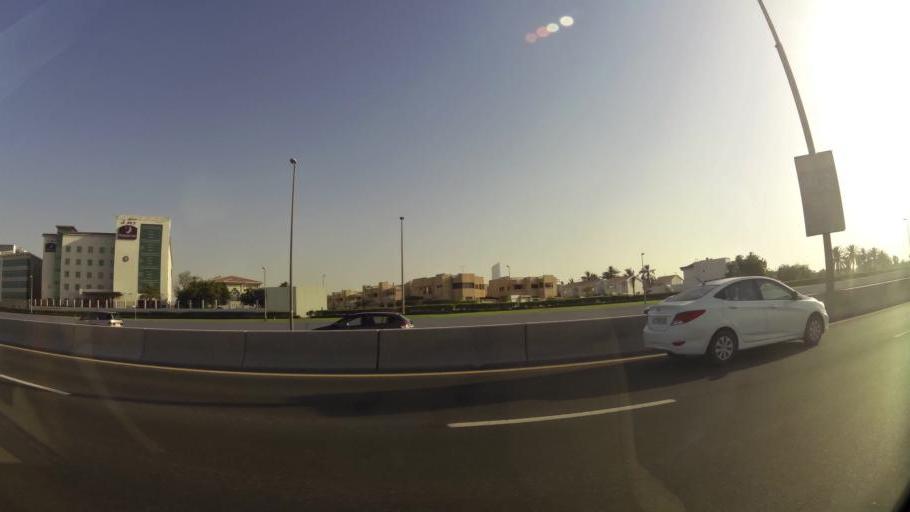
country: AE
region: Ash Shariqah
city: Sharjah
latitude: 25.2444
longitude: 55.3583
